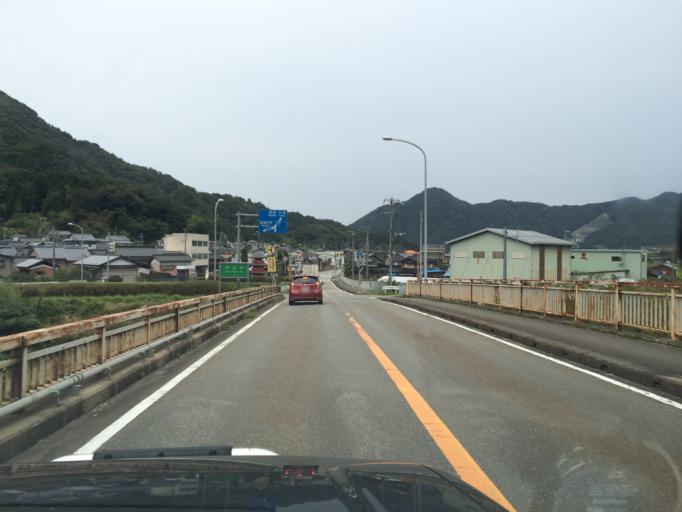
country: JP
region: Hyogo
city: Toyooka
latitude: 35.4194
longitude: 134.7913
